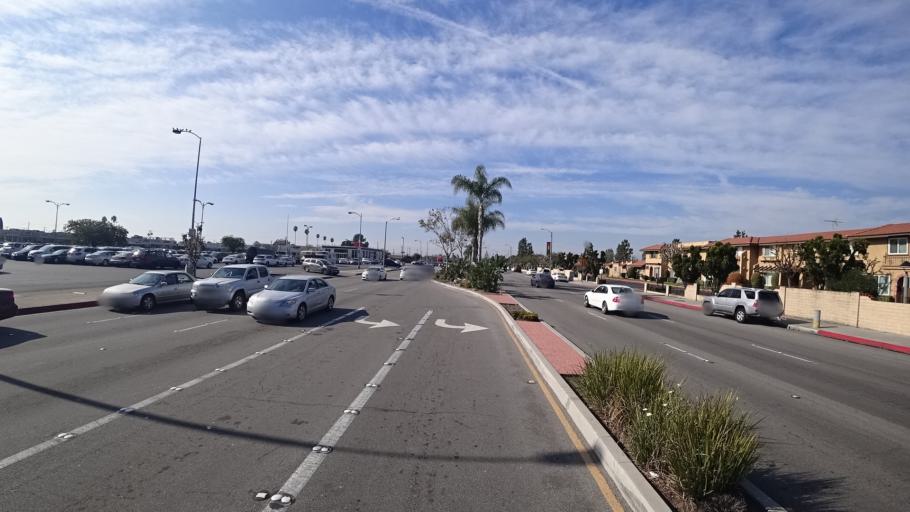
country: US
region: California
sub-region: Orange County
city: Midway City
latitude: 33.7448
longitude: -117.9730
